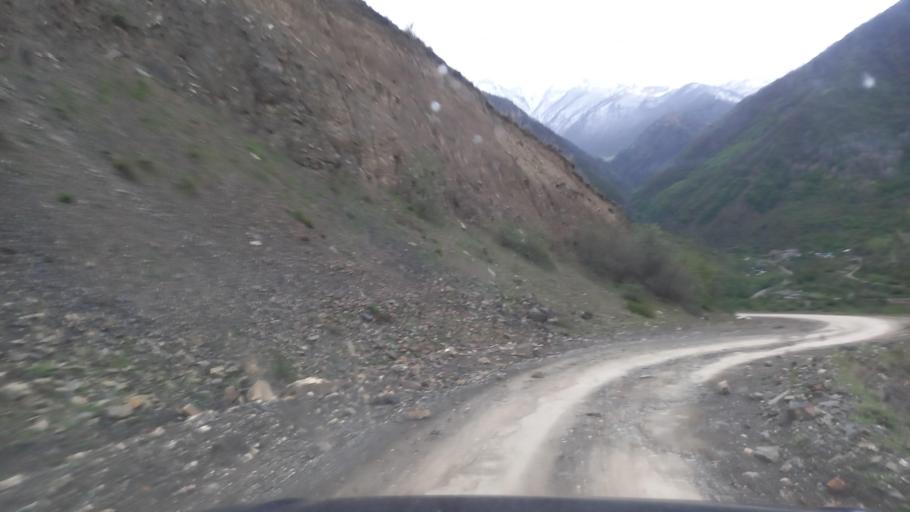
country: RU
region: North Ossetia
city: Mizur
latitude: 42.8565
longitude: 44.1578
